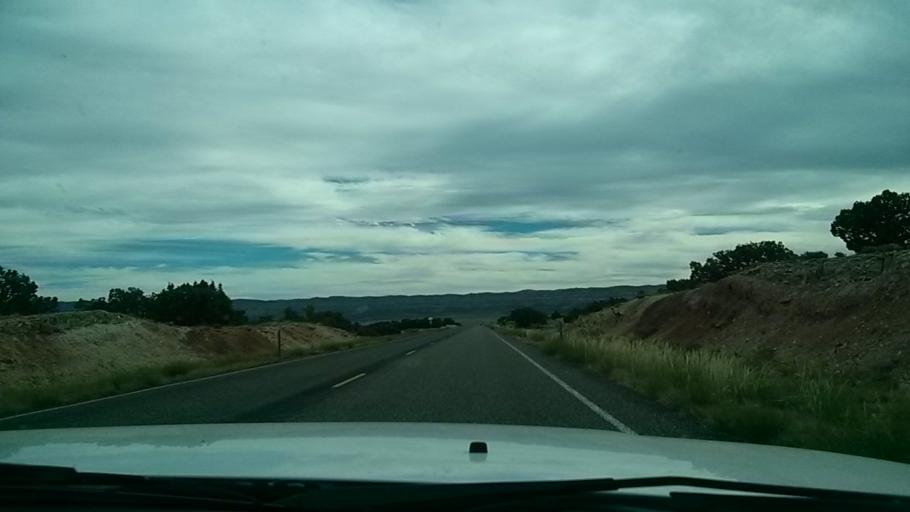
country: US
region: Utah
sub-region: Wayne County
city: Loa
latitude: 37.7352
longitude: -111.5121
